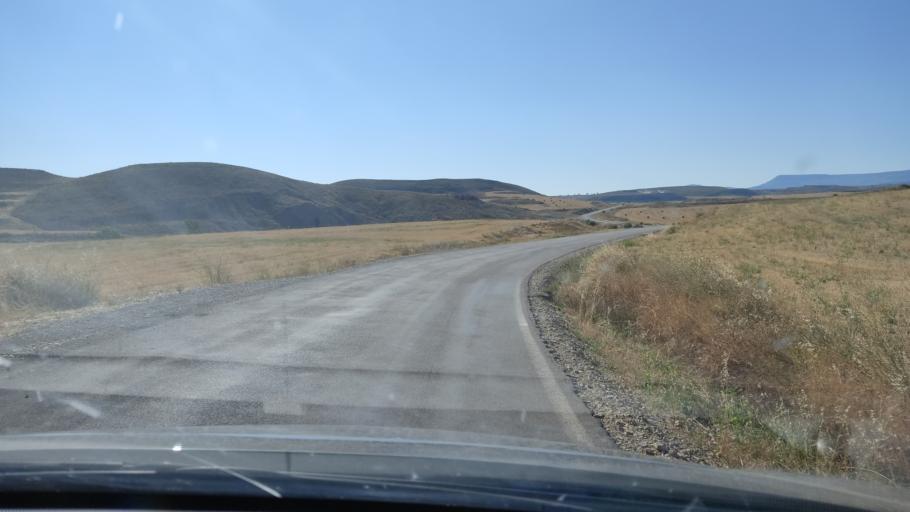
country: ES
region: Aragon
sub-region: Provincia de Teruel
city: Monforte de Moyuela
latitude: 41.0505
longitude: -1.0091
